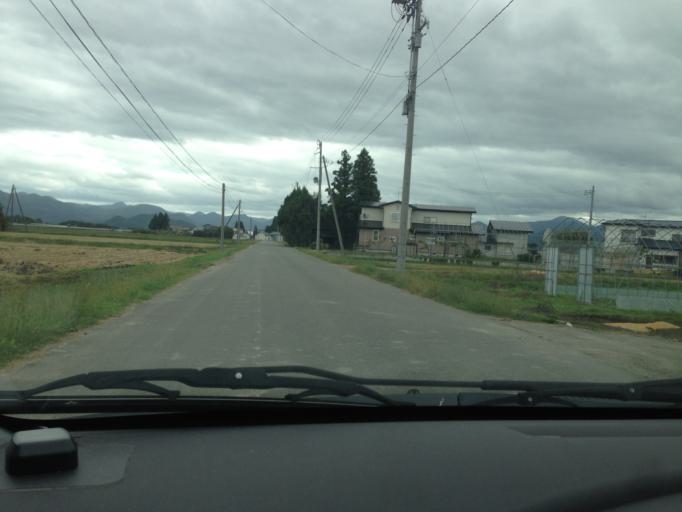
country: JP
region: Fukushima
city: Kitakata
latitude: 37.4840
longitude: 139.8462
